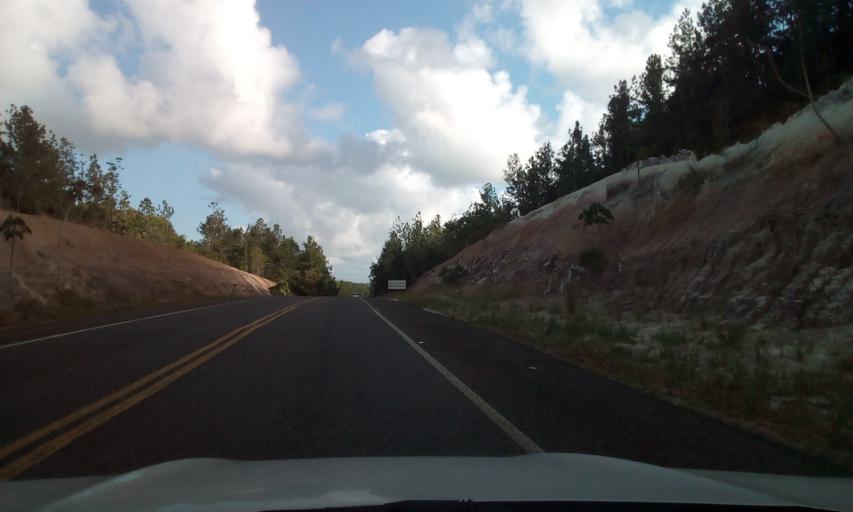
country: BR
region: Bahia
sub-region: Entre Rios
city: Entre Rios
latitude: -12.1146
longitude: -37.7866
